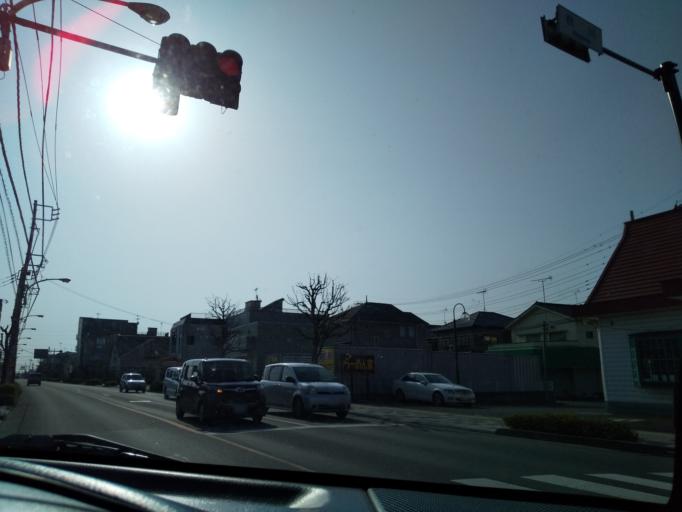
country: JP
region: Tokyo
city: Fussa
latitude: 35.7288
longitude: 139.2893
